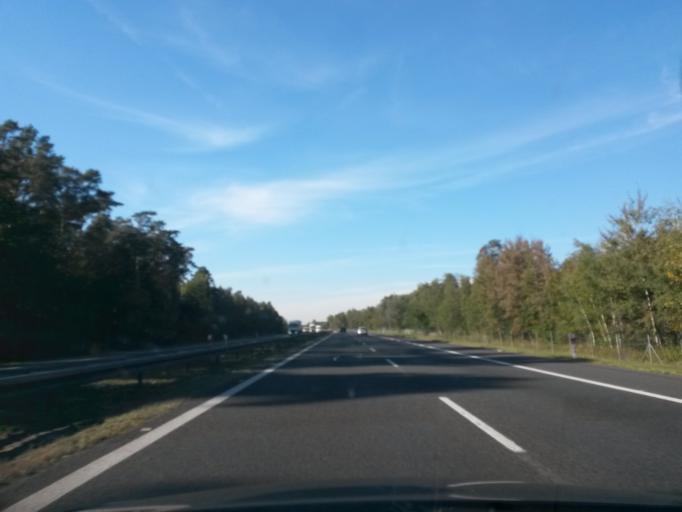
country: PL
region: Opole Voivodeship
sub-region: Powiat brzeski
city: Lewin Brzeski
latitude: 50.7001
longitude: 17.6198
